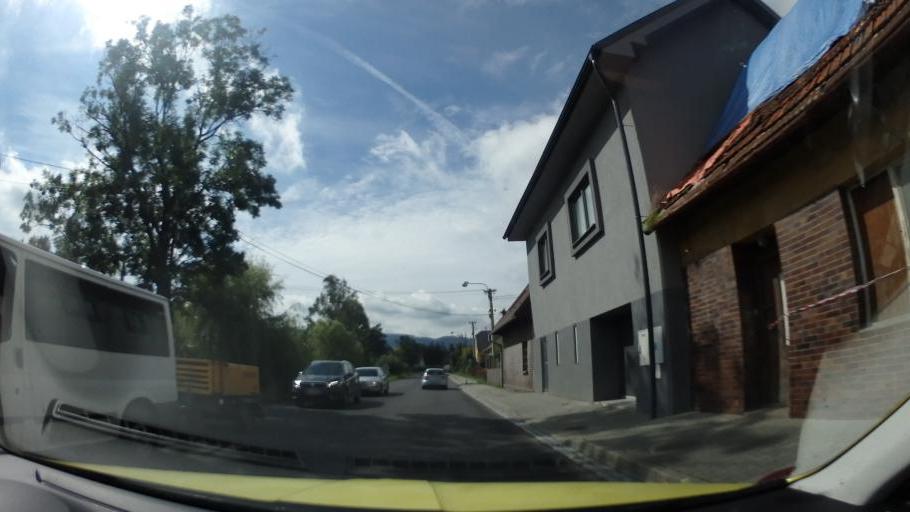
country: CZ
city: Hodslavice
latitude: 49.5498
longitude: 18.0261
